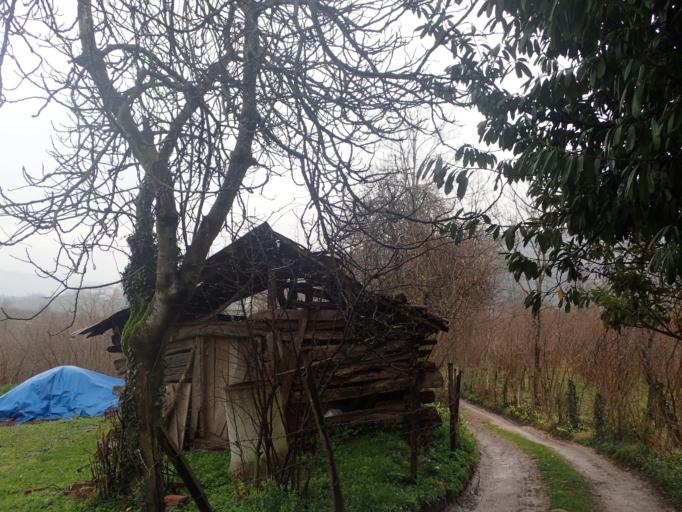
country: TR
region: Ordu
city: Camas
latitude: 40.9528
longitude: 37.5133
